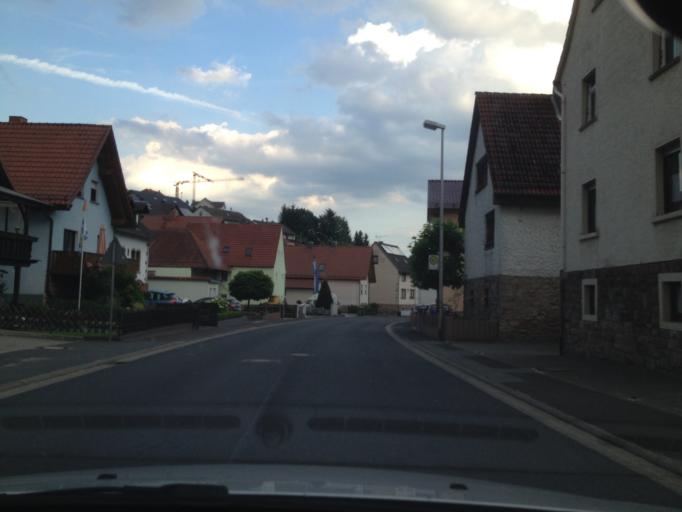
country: DE
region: Bavaria
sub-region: Regierungsbezirk Unterfranken
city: Weibersbrunn
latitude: 49.9340
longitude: 9.3632
